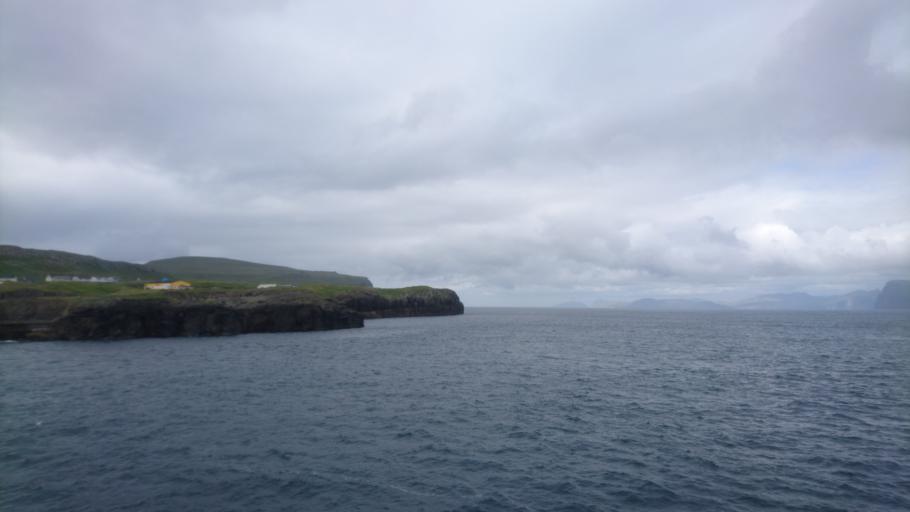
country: FO
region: Sandoy
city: Sandur
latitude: 61.9060
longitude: -6.8757
